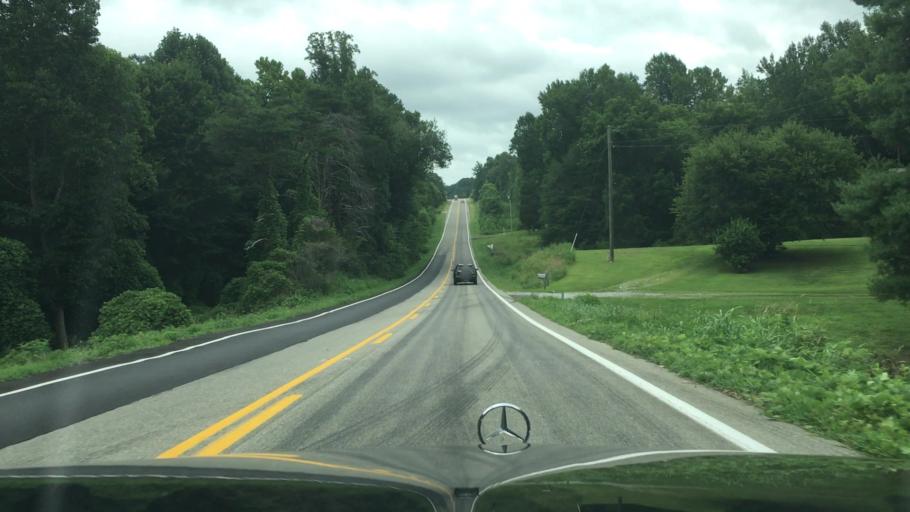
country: US
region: Virginia
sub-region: Prince Edward County
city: Farmville
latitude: 37.2745
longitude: -78.2462
